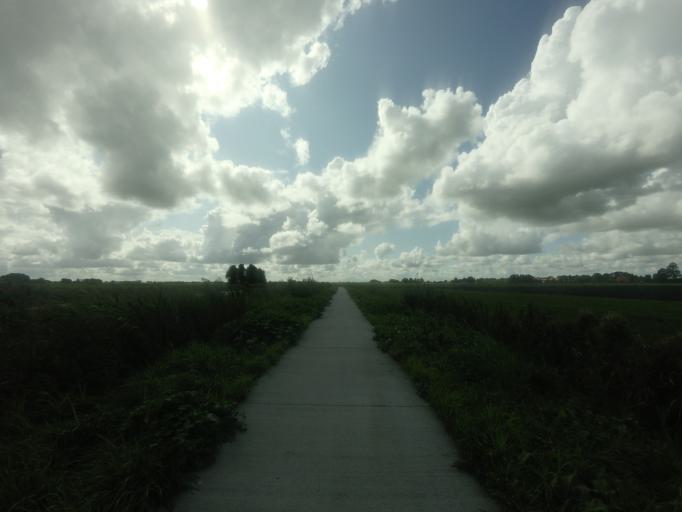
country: NL
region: Friesland
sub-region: Gemeente Littenseradiel
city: Makkum
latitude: 53.0911
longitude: 5.7104
